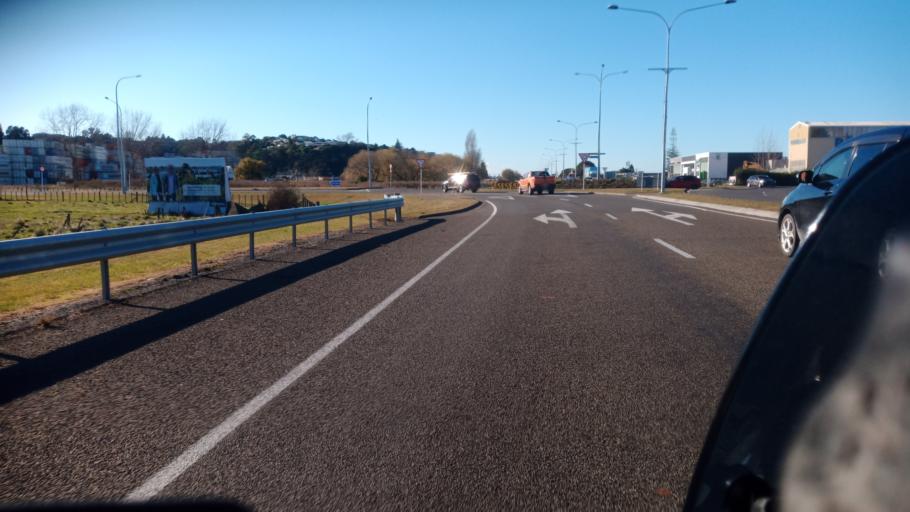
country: NZ
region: Hawke's Bay
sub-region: Napier City
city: Napier
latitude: -39.4962
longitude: 176.8846
